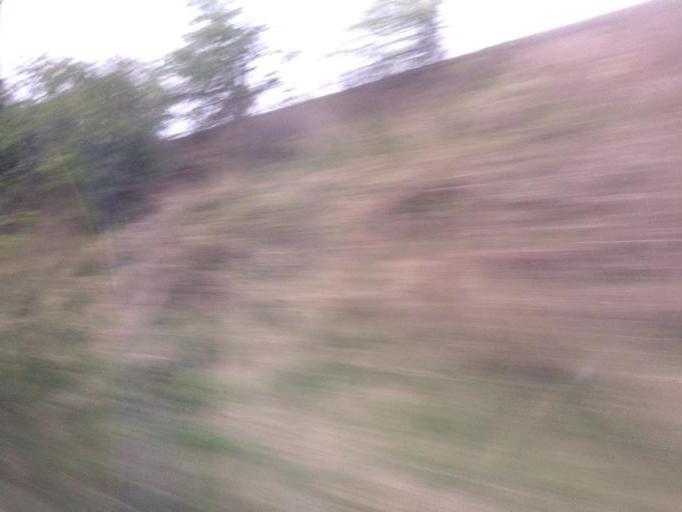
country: GB
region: Scotland
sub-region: North Lanarkshire
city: Chryston
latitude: 55.9354
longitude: -4.0892
